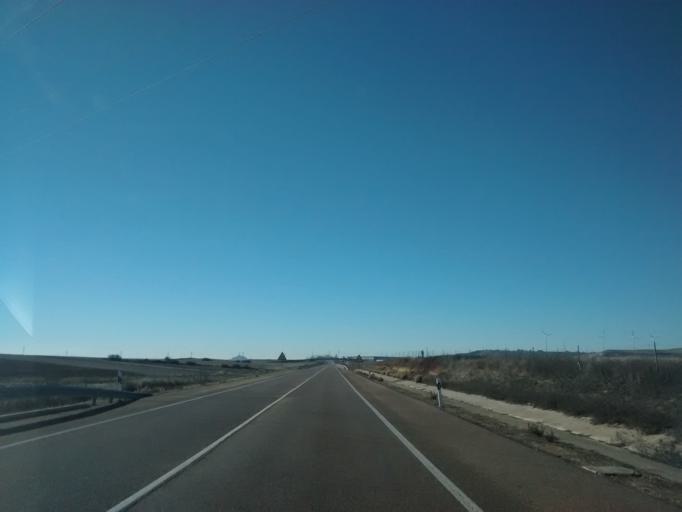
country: ES
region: Castille and Leon
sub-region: Provincia de Palencia
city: Fuentes de Valdepero
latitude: 42.0584
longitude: -4.4961
